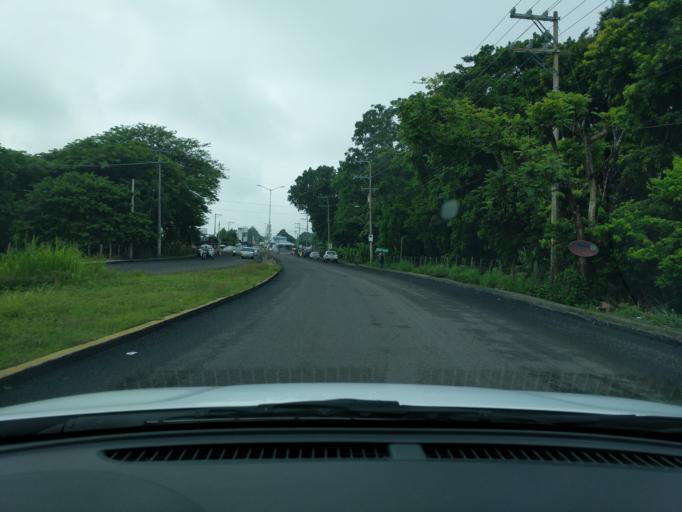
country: MX
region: Tabasco
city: Villahermosa
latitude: 17.9630
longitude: -92.9638
